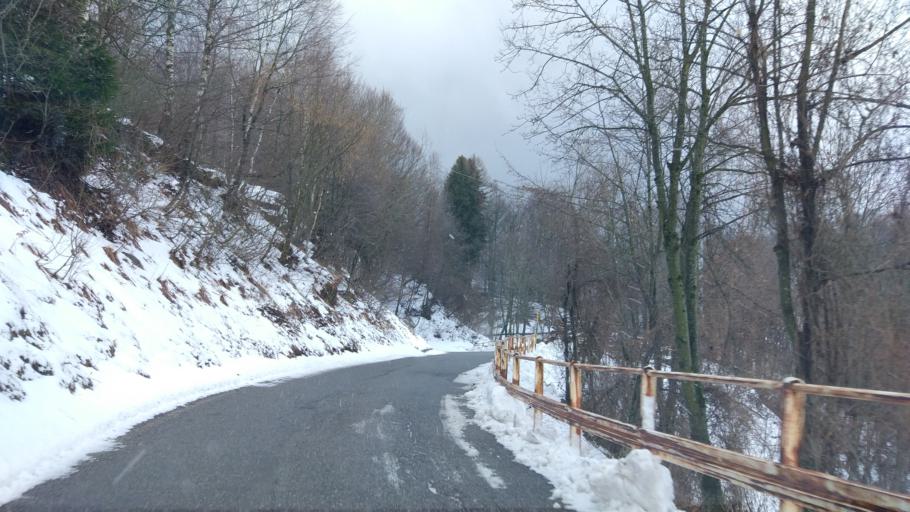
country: IT
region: Lombardy
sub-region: Provincia di Lecco
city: Moggio
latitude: 45.9038
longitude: 9.4951
